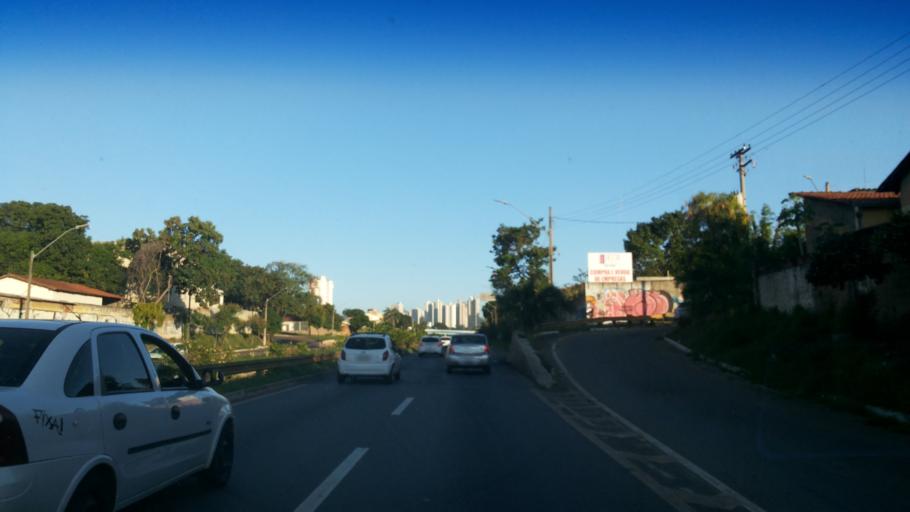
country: BR
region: Goias
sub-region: Goiania
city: Goiania
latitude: -16.6805
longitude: -49.2486
